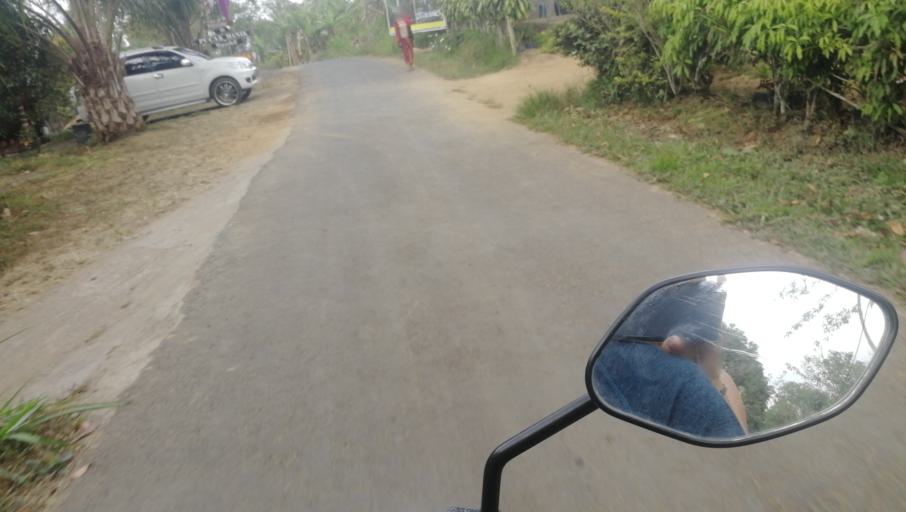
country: ID
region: Bali
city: Banjar Ambengan
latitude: -8.2121
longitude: 115.1101
